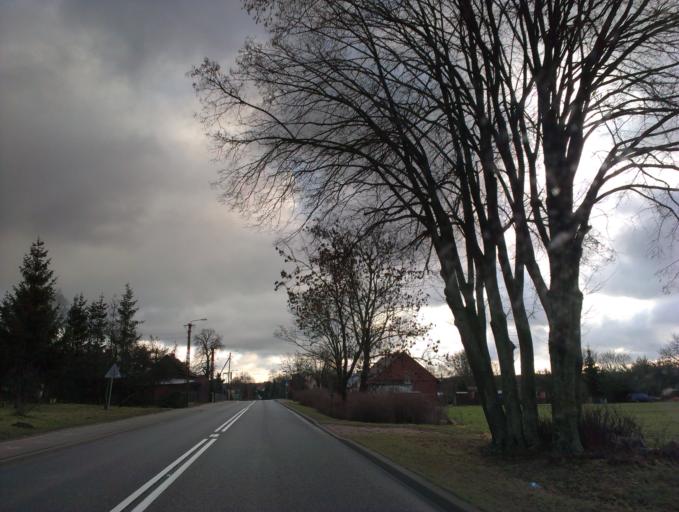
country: PL
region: Pomeranian Voivodeship
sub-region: Powiat czluchowski
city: Debrzno
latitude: 53.6258
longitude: 17.2255
